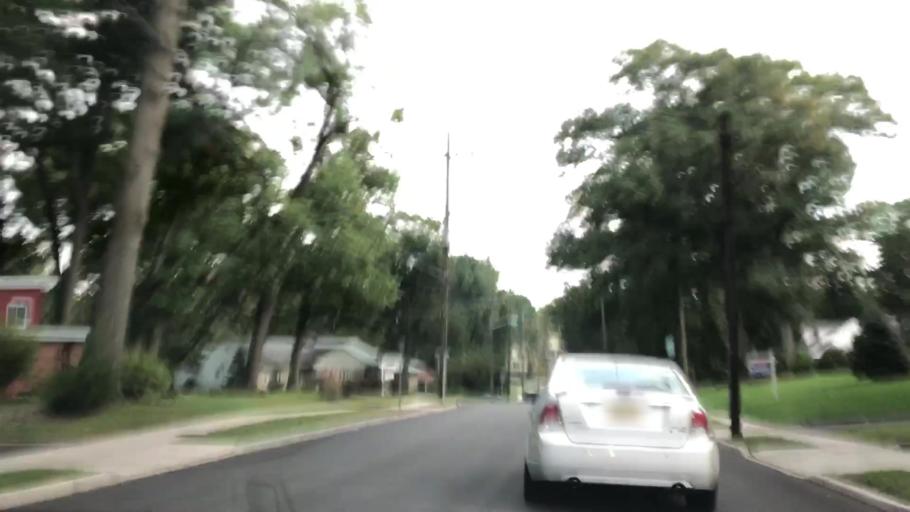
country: US
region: New Jersey
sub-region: Essex County
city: Upper Montclair
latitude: 40.8573
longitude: -74.1930
